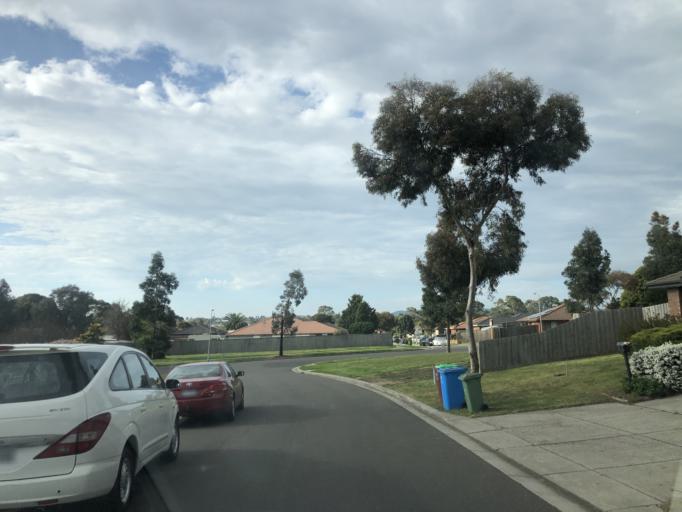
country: AU
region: Victoria
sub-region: Casey
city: Hampton Park
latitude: -38.0227
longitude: 145.2536
